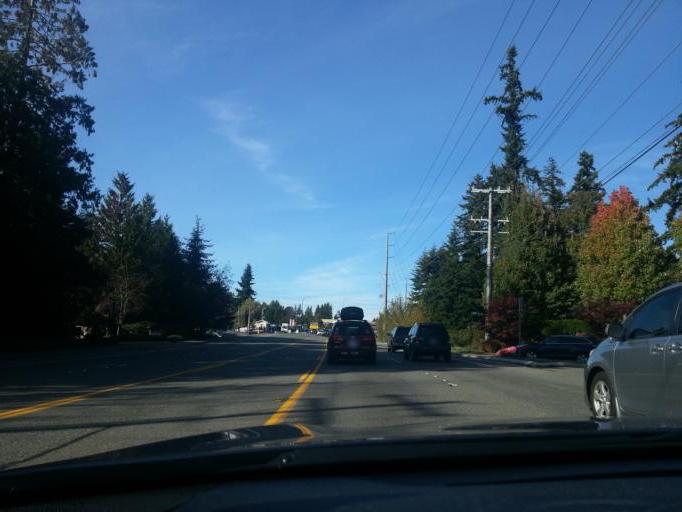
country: US
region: Washington
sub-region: Snohomish County
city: North Creek
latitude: 47.8260
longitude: -122.2079
